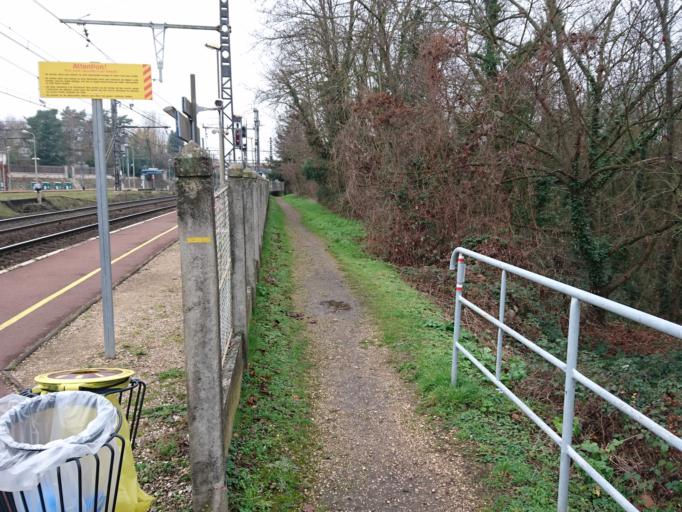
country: FR
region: Ile-de-France
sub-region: Departement de Seine-et-Marne
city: Veneux-les-Sablons
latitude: 48.3788
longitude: 2.7990
